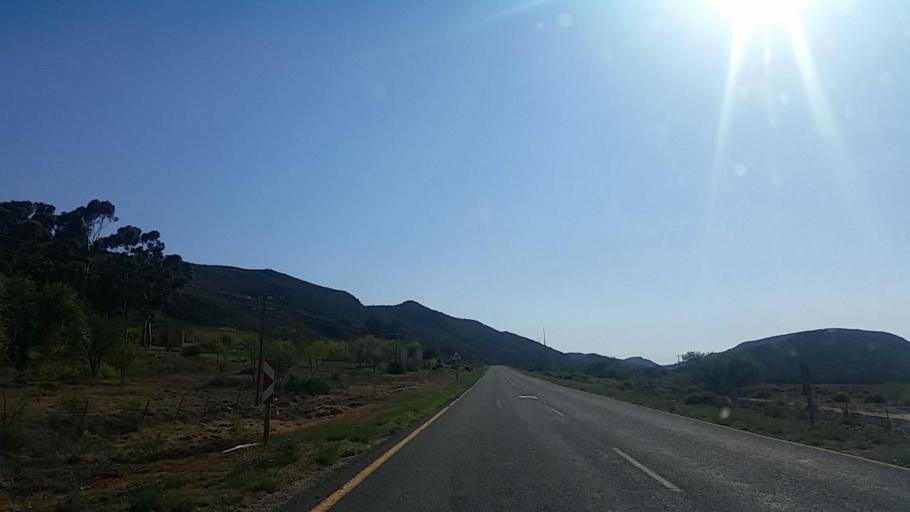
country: ZA
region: Eastern Cape
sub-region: Cacadu District Municipality
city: Willowmore
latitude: -33.3942
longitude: 23.3660
